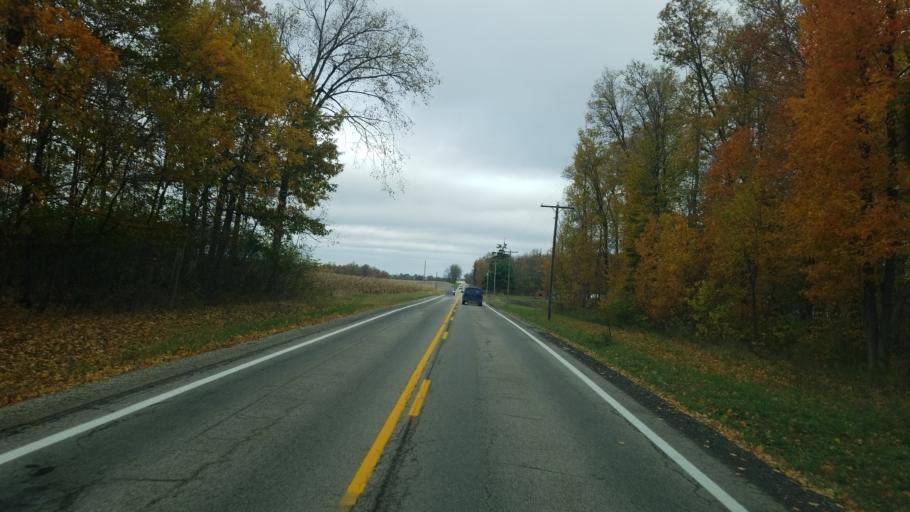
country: US
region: Ohio
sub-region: Crawford County
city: Bucyrus
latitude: 40.8617
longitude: -82.8554
